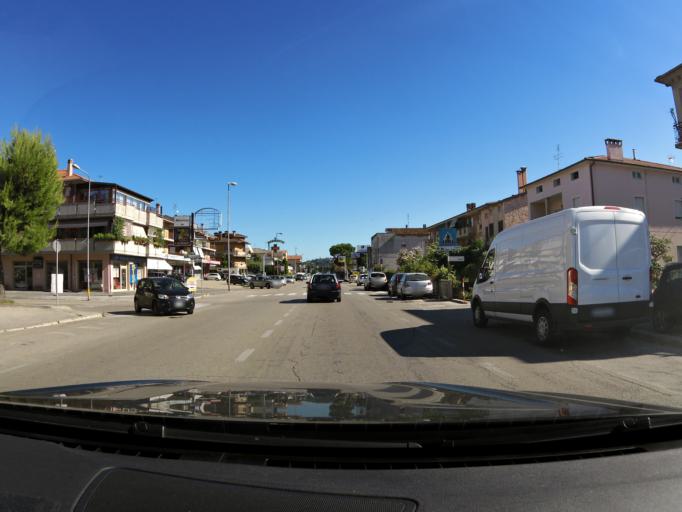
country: IT
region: The Marches
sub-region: Province of Fermo
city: Porto San Giorgio
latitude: 43.1689
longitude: 13.7986
